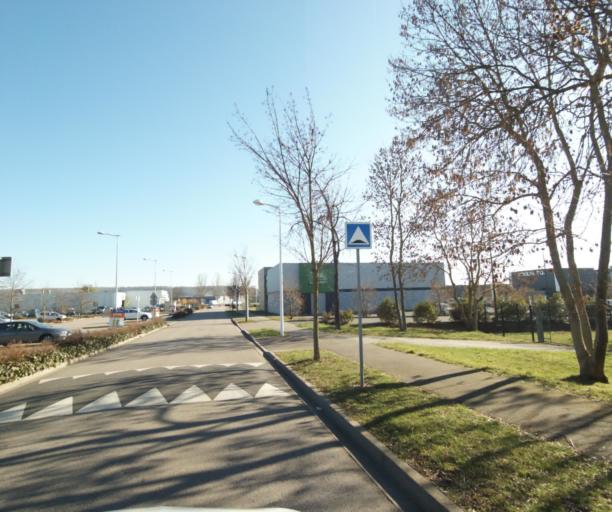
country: FR
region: Lorraine
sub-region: Departement de Meurthe-et-Moselle
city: Pulnoy
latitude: 48.7113
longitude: 6.2464
